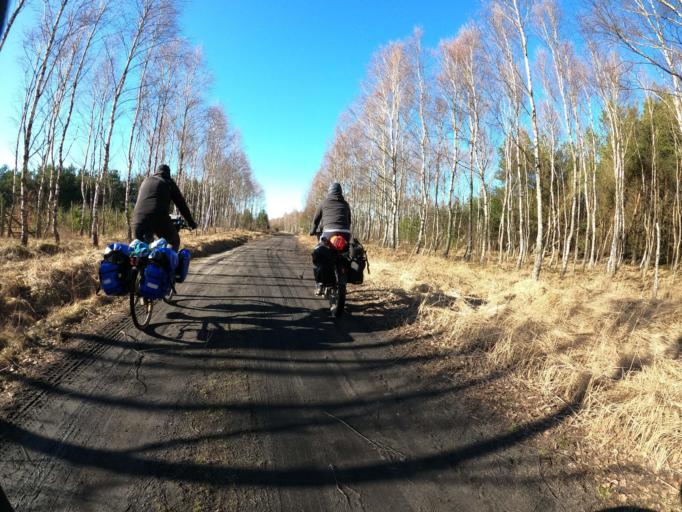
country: PL
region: West Pomeranian Voivodeship
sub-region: Powiat szczecinecki
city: Borne Sulinowo
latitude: 53.5467
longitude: 16.5625
